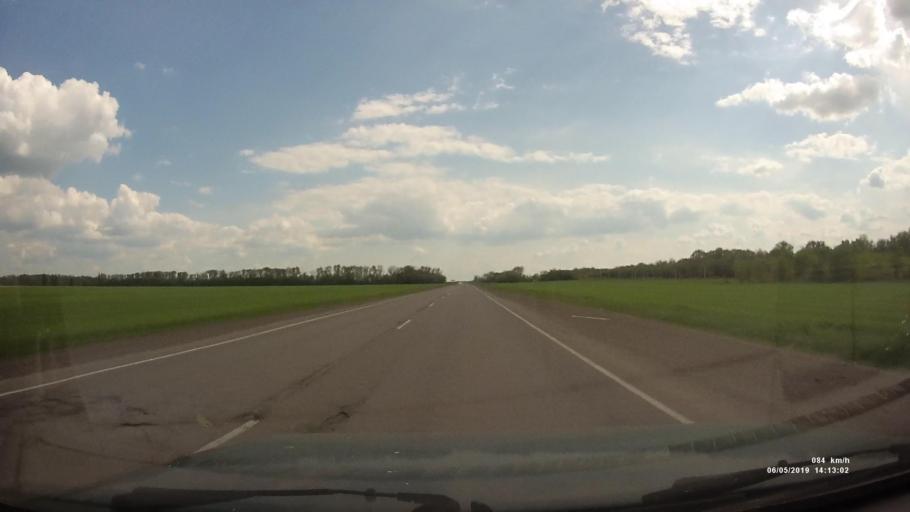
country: RU
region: Rostov
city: Kamenolomni
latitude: 47.6682
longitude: 40.2892
